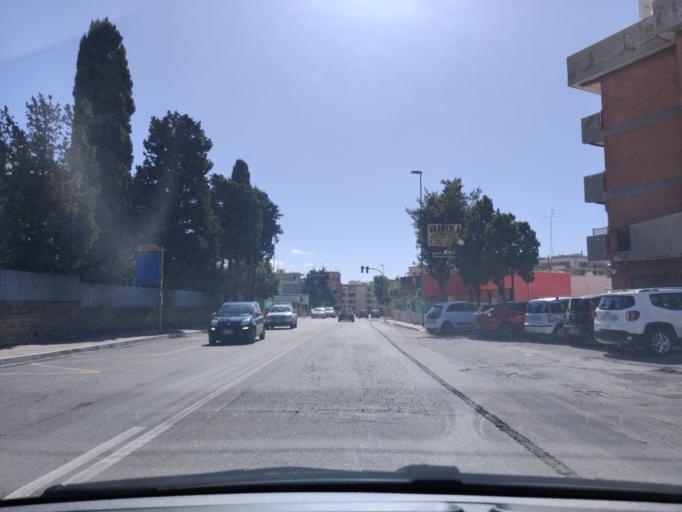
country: IT
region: Latium
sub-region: Citta metropolitana di Roma Capitale
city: Civitavecchia
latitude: 42.0909
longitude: 11.8072
